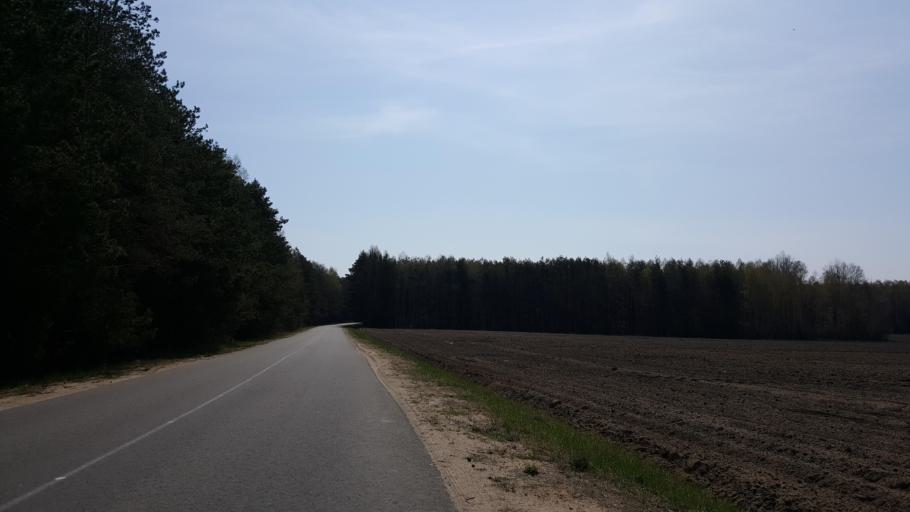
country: BY
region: Brest
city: Kamyanyets
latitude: 52.3620
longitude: 23.8135
